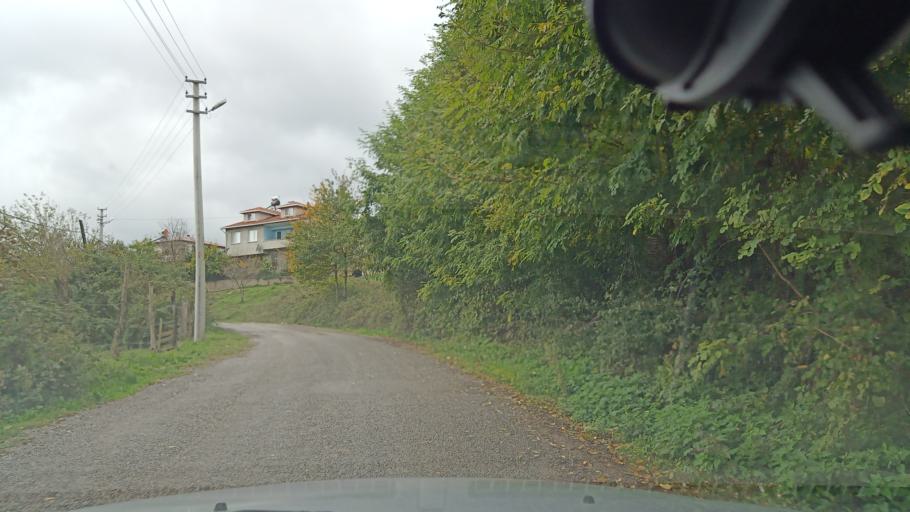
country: TR
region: Sakarya
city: Karasu
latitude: 41.0894
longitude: 30.5893
